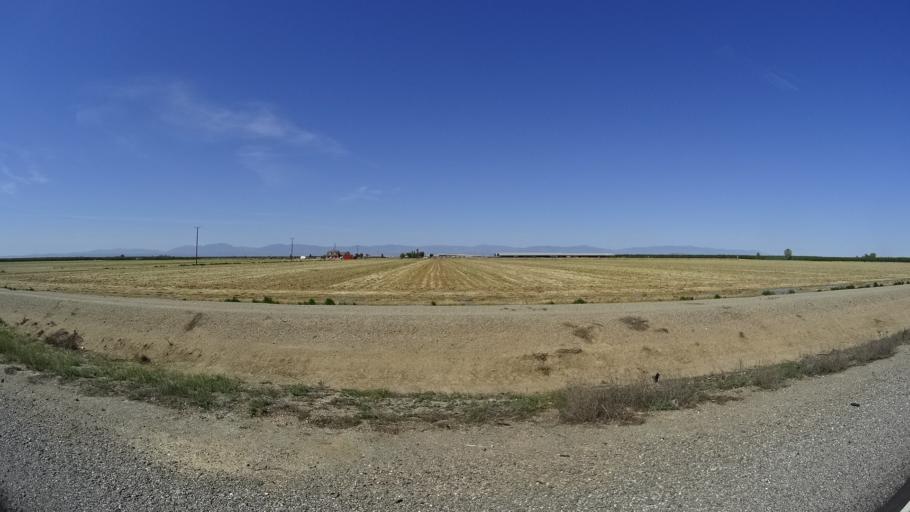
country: US
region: California
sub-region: Glenn County
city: Orland
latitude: 39.6569
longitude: -122.1407
